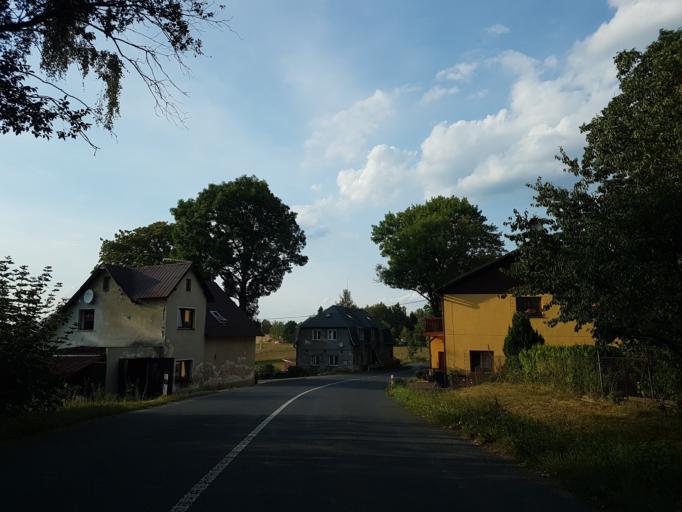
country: CZ
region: Liberecky
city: Mala Skala
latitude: 50.6672
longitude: 15.1800
